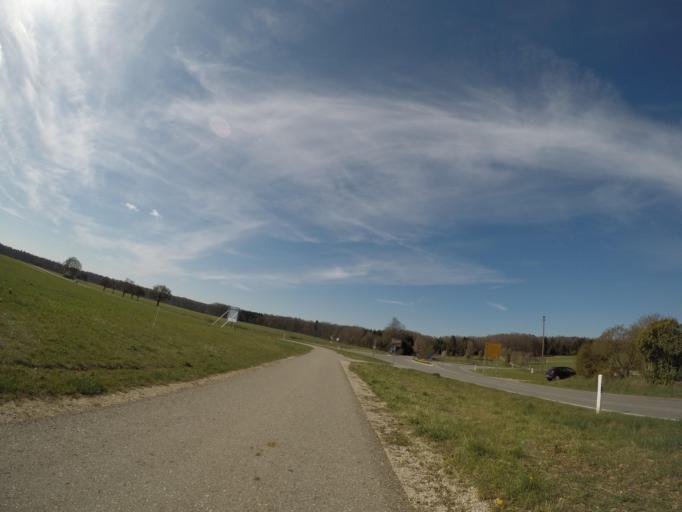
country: DE
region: Baden-Wuerttemberg
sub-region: Tuebingen Region
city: Mehrstetten
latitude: 48.3291
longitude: 9.6006
